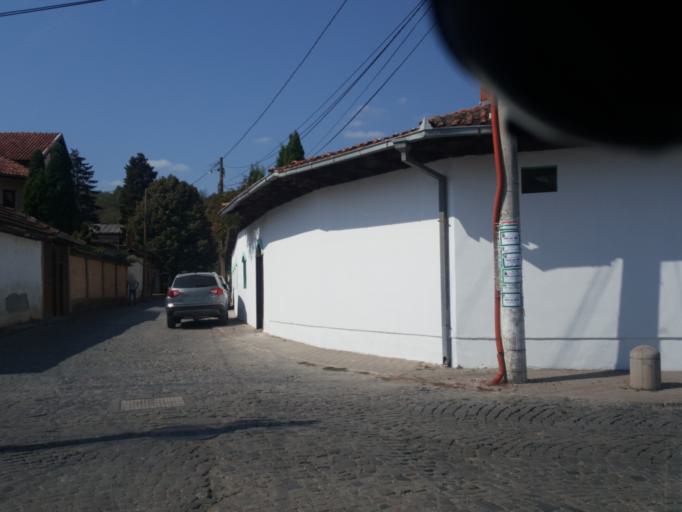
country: XK
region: Gjakova
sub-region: Komuna e Gjakoves
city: Gjakove
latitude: 42.3782
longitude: 20.4278
